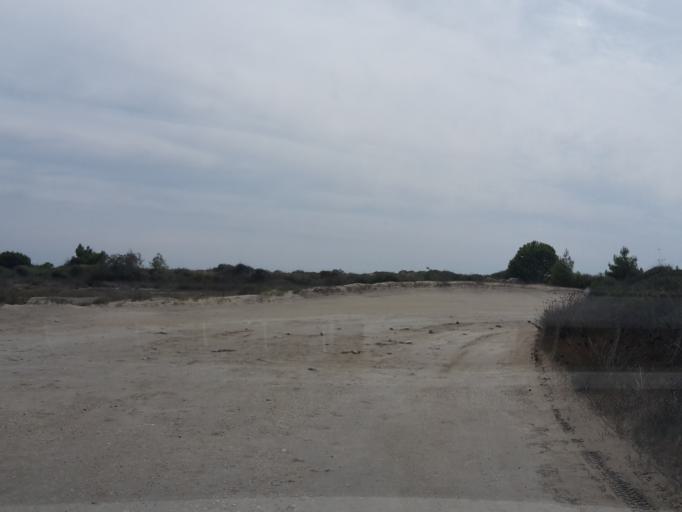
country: FR
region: Provence-Alpes-Cote d'Azur
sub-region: Departement des Bouches-du-Rhone
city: Saintes-Maries-de-la-Mer
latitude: 43.4094
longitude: 4.6057
